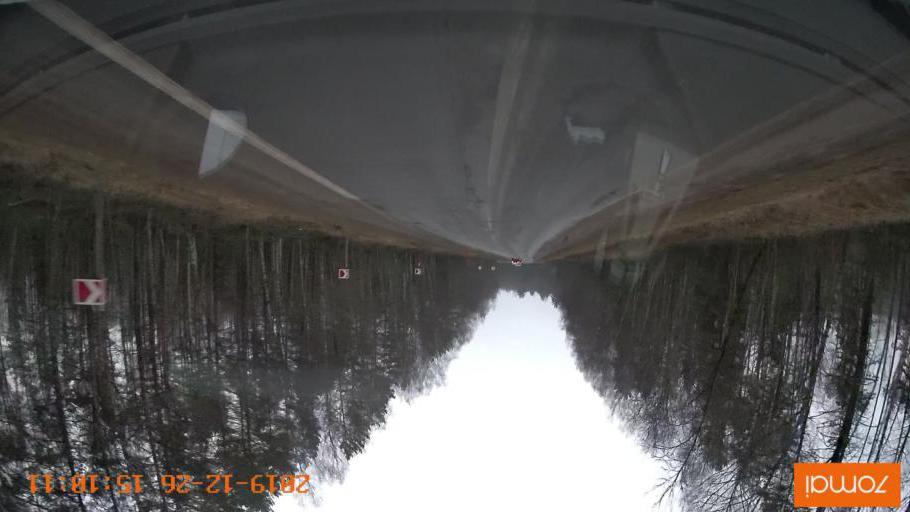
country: RU
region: Jaroslavl
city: Rybinsk
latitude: 58.1423
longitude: 38.8485
